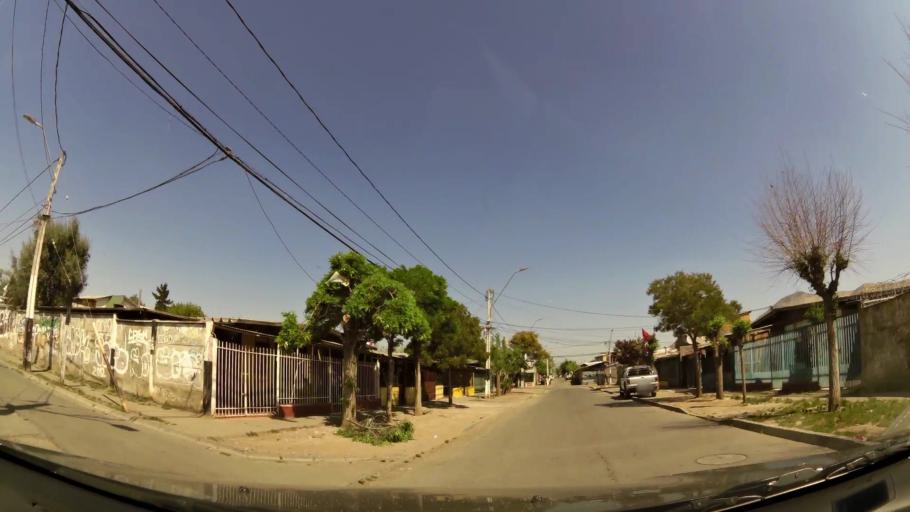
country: CL
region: Santiago Metropolitan
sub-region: Provincia de Maipo
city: San Bernardo
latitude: -33.5784
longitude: -70.7044
